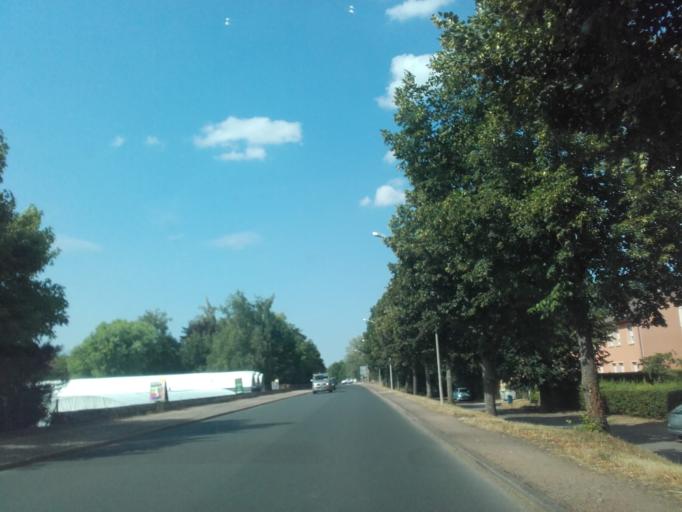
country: FR
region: Bourgogne
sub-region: Departement de Saone-et-Loire
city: Cluny
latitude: 46.4304
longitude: 4.6630
